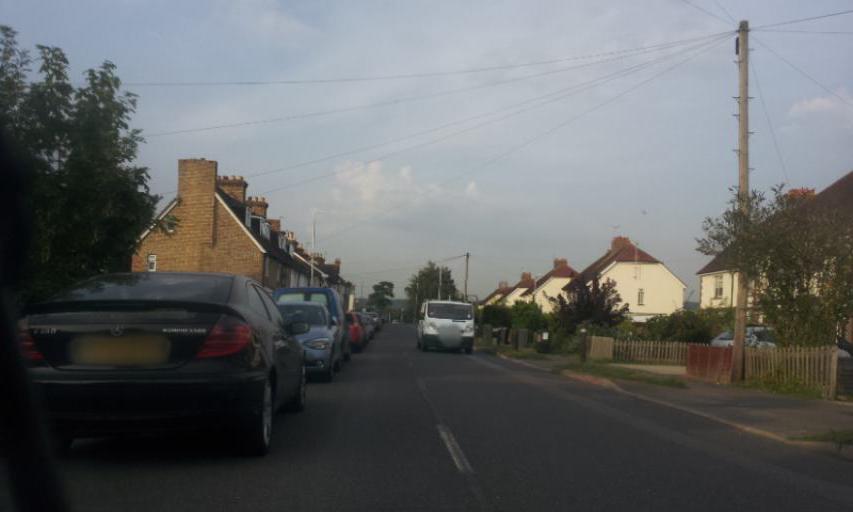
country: GB
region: England
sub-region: Kent
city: Larkfield
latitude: 51.2966
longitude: 0.4529
